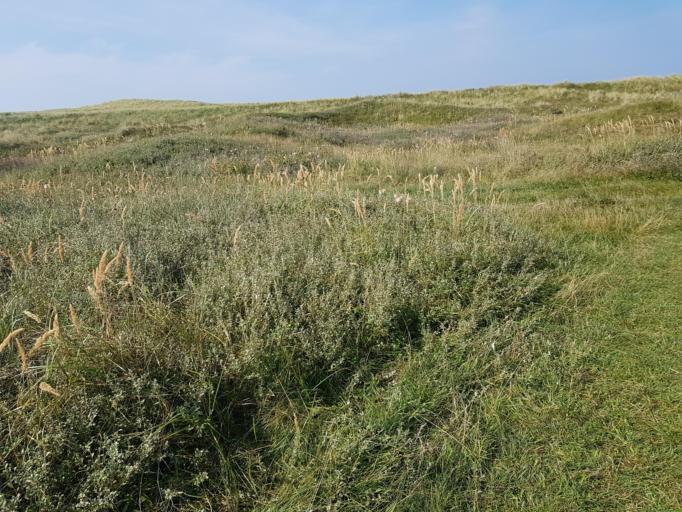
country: NL
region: North Holland
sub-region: Gemeente Texel
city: Den Burg
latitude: 53.1713
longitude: 4.8354
